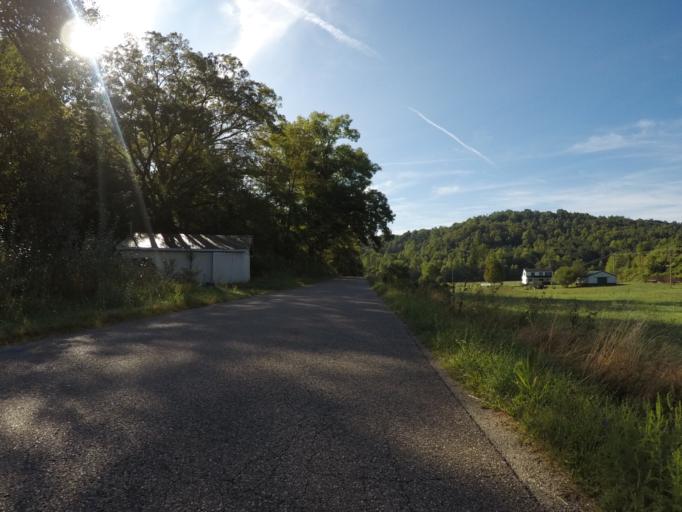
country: US
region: Ohio
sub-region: Lawrence County
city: Burlington
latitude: 38.5012
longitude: -82.5127
